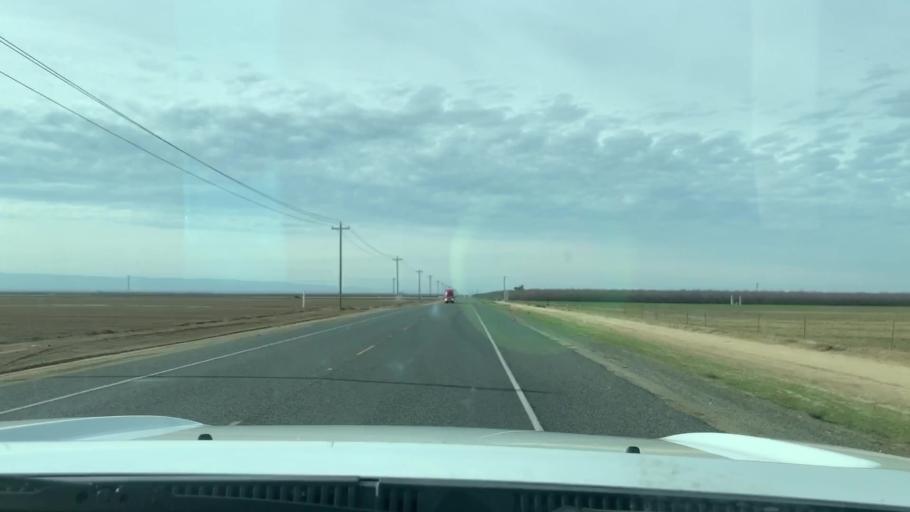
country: US
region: California
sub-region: Kern County
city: Lost Hills
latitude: 35.6013
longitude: -119.5499
